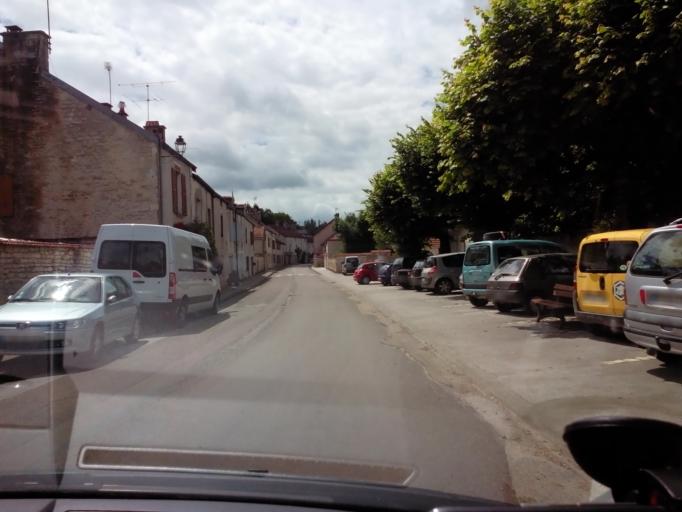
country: FR
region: Champagne-Ardenne
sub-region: Departement de la Haute-Marne
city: Chateauvillain
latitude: 47.9475
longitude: 5.0104
